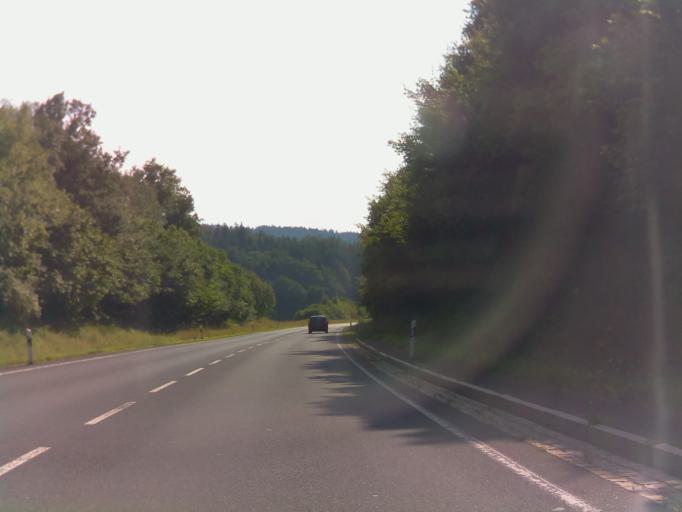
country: DE
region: Bavaria
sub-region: Regierungsbezirk Unterfranken
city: Wildflecken
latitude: 50.3848
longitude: 9.9325
